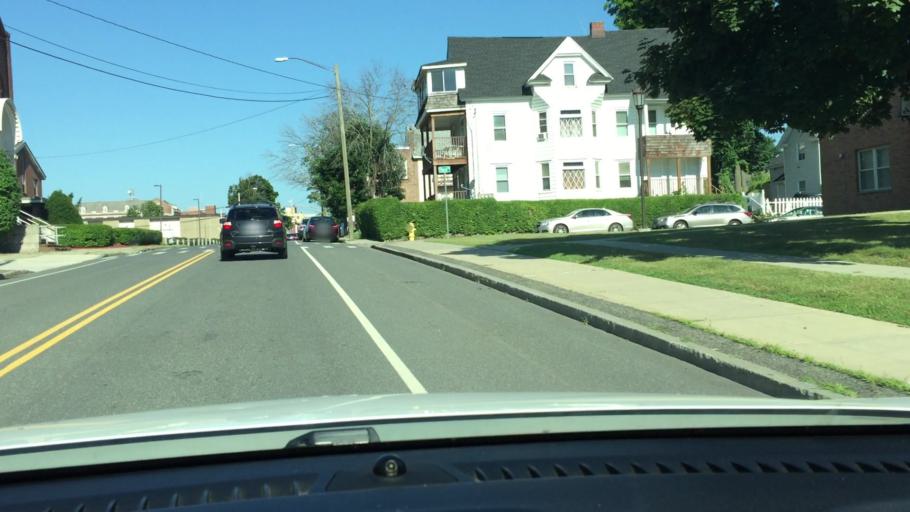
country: US
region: Massachusetts
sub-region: Berkshire County
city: Pittsfield
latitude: 42.4491
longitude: -73.2461
